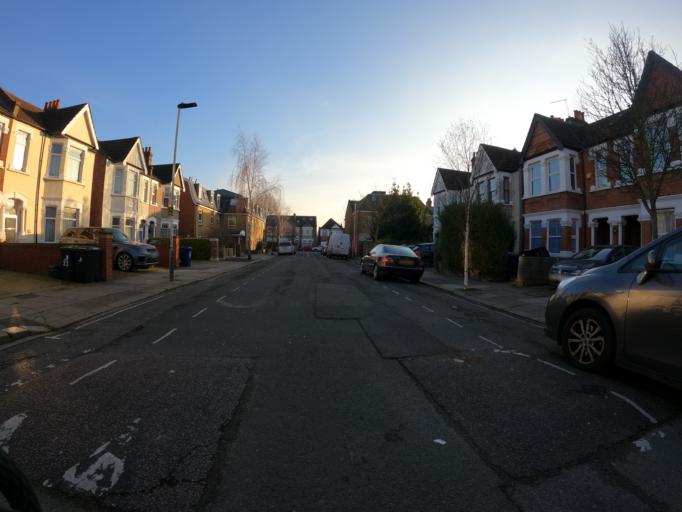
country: GB
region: England
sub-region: Greater London
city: Ealing
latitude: 51.5088
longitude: -0.3244
